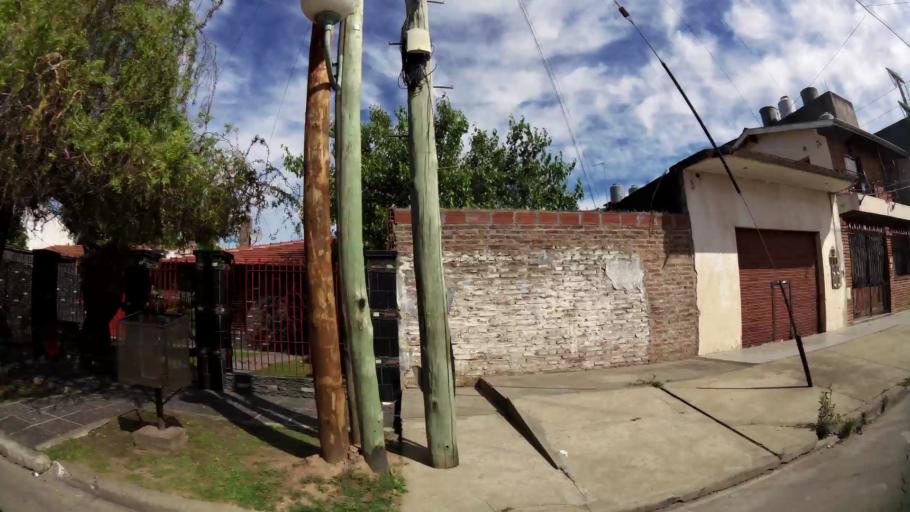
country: AR
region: Buenos Aires
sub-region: Partido de Almirante Brown
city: Adrogue
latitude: -34.7861
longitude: -58.3145
